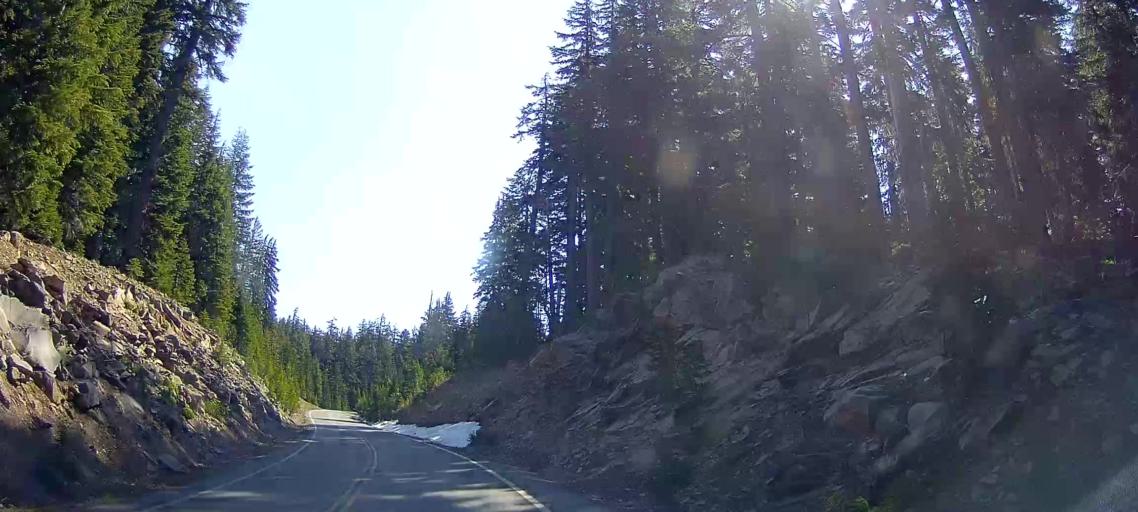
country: US
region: Oregon
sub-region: Klamath County
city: Klamath Falls
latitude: 42.8793
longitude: -122.1213
